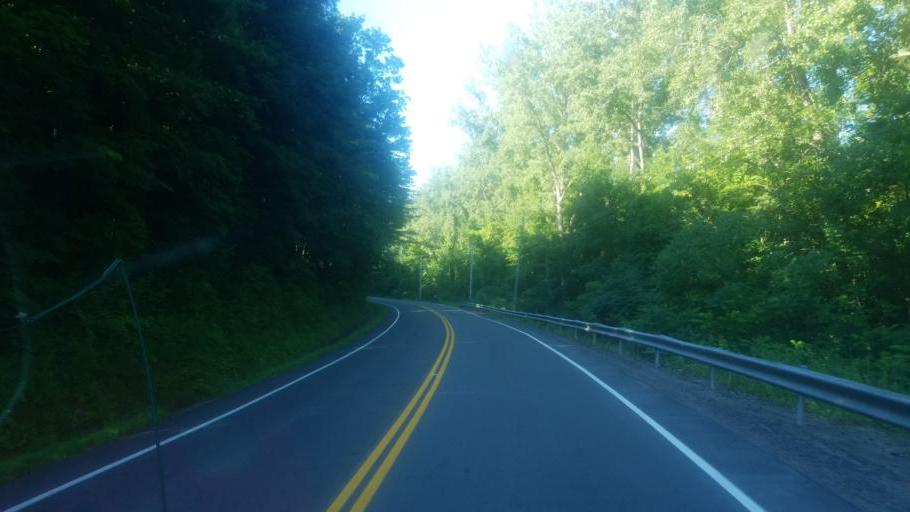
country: US
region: New York
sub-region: Wayne County
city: Newark
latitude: 43.0908
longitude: -77.0647
